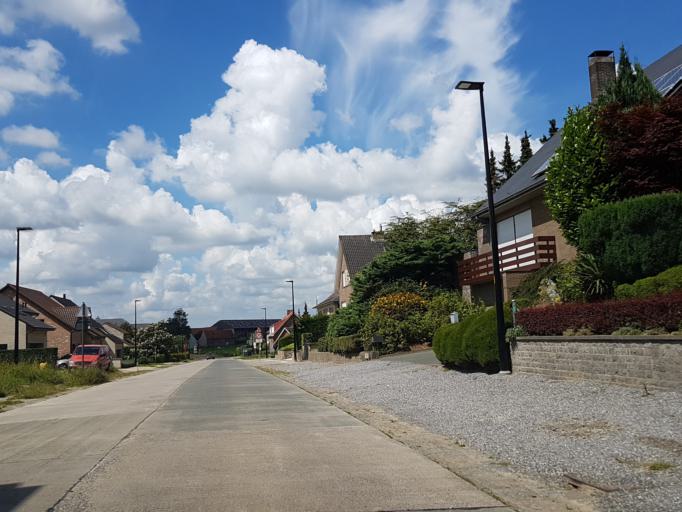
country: BE
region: Flanders
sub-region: Provincie Vlaams-Brabant
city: Wemmel
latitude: 50.9086
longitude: 4.2928
